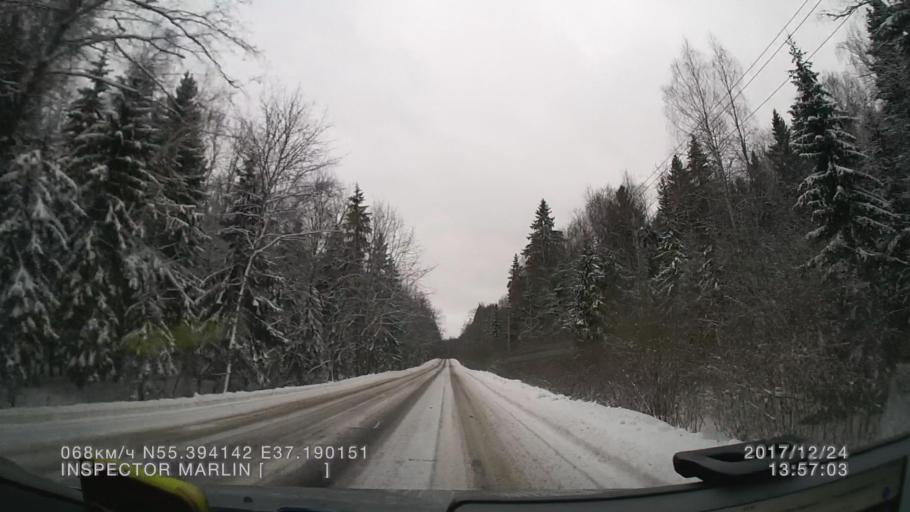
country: RU
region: Moskovskaya
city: Troitsk
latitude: 55.3940
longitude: 37.1898
